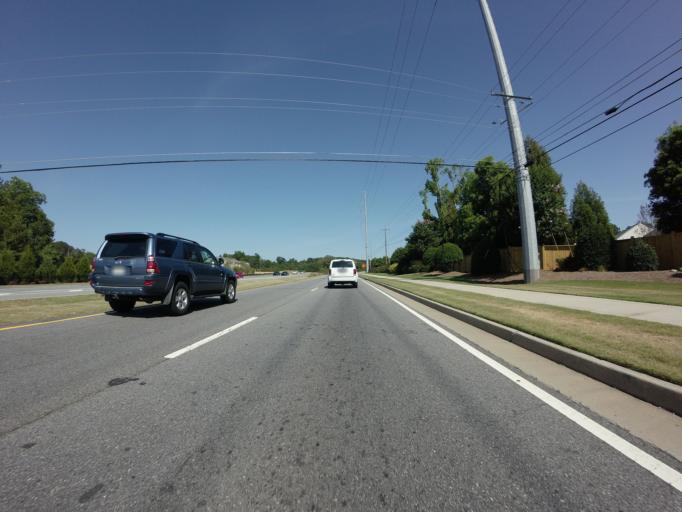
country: US
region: Georgia
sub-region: Gwinnett County
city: Duluth
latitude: 34.0538
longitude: -84.1258
